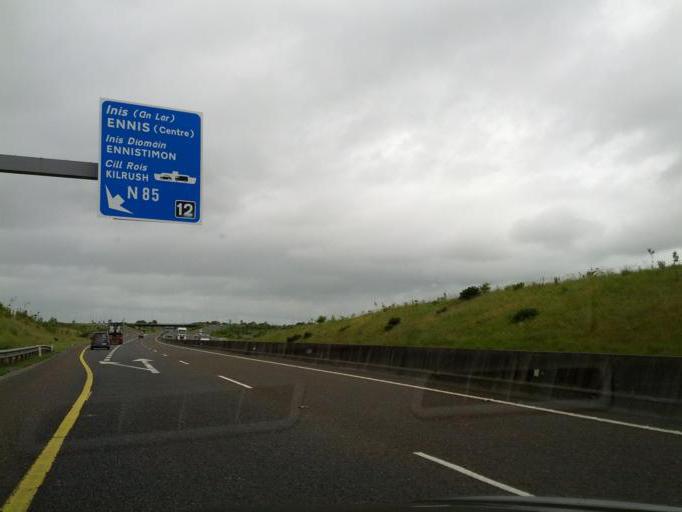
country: IE
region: Munster
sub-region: An Clar
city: Ennis
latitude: 52.8216
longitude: -8.9381
